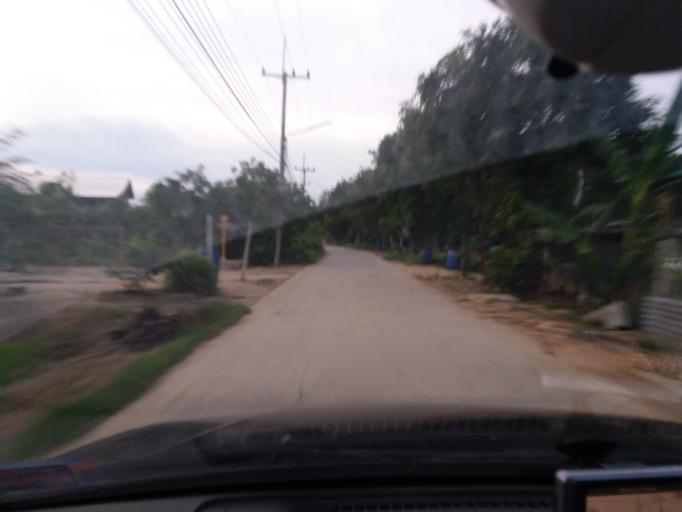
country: TH
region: Suphan Buri
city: Doembang Nangbuat
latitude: 14.8309
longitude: 100.1343
